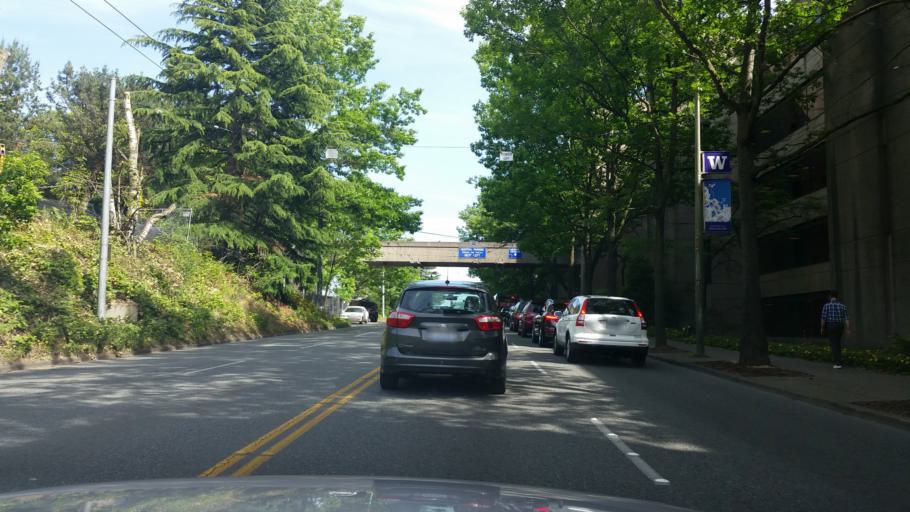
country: US
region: Washington
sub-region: King County
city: Seattle
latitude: 47.6515
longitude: -122.3097
